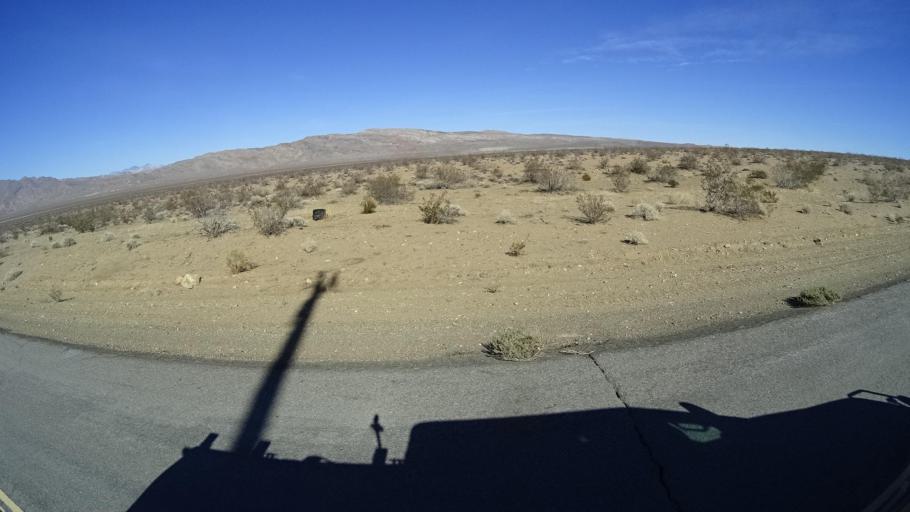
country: US
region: California
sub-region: Kern County
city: Ridgecrest
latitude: 35.3829
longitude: -117.7077
